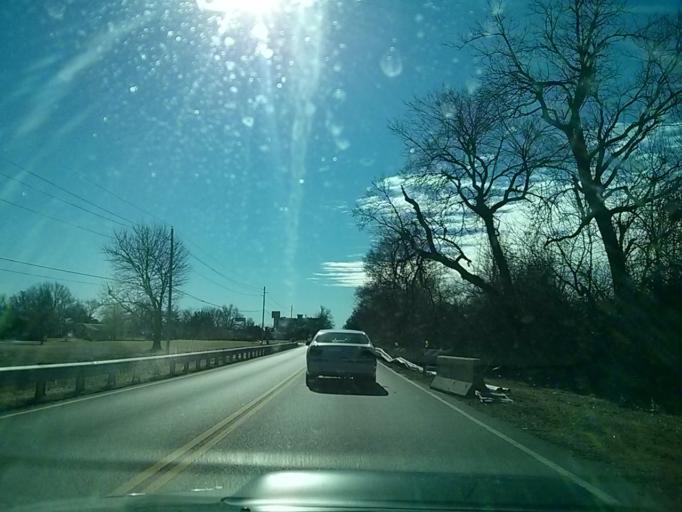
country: US
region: Oklahoma
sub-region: Tulsa County
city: Jenks
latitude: 36.0414
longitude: -95.9577
